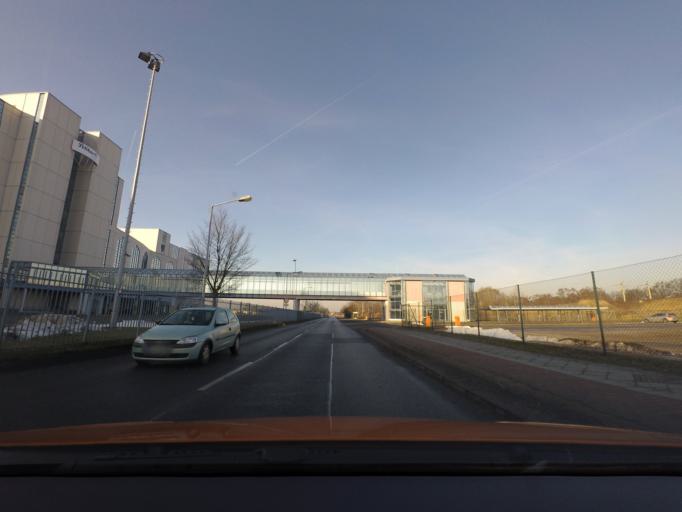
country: DE
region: Brandenburg
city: Falkensee
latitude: 52.5517
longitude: 13.1154
